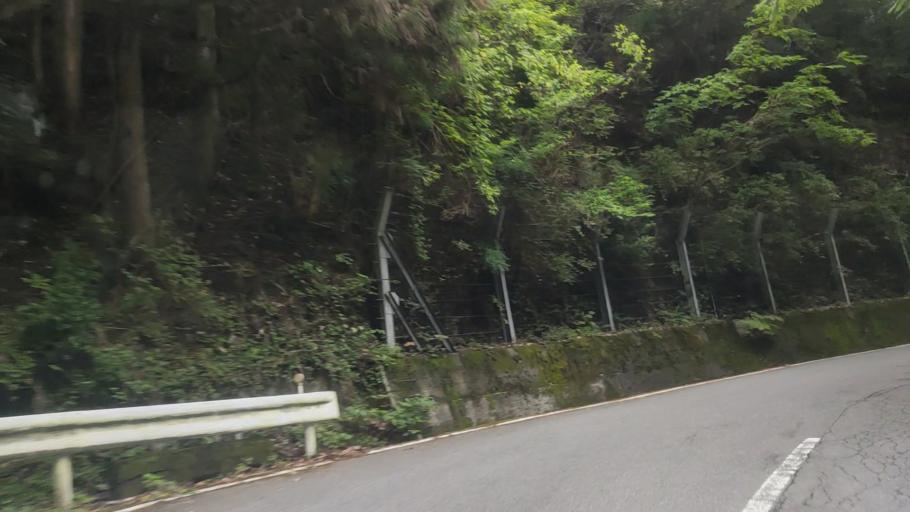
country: JP
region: Wakayama
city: Koya
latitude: 34.2115
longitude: 135.5472
